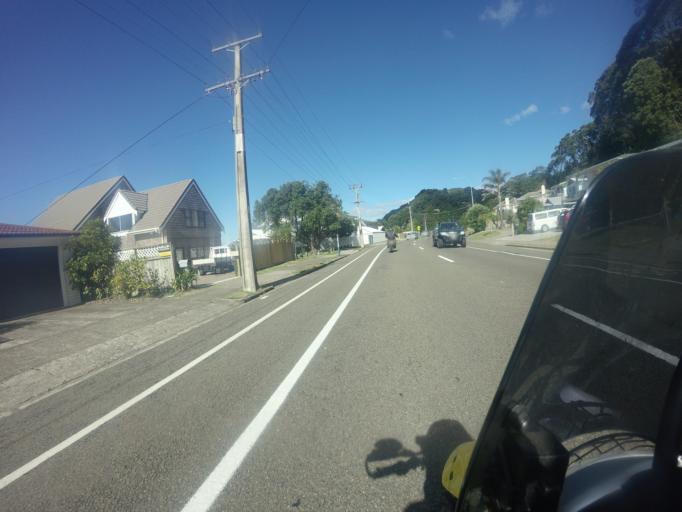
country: NZ
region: Bay of Plenty
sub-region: Whakatane District
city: Whakatane
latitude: -37.9680
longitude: 177.0473
